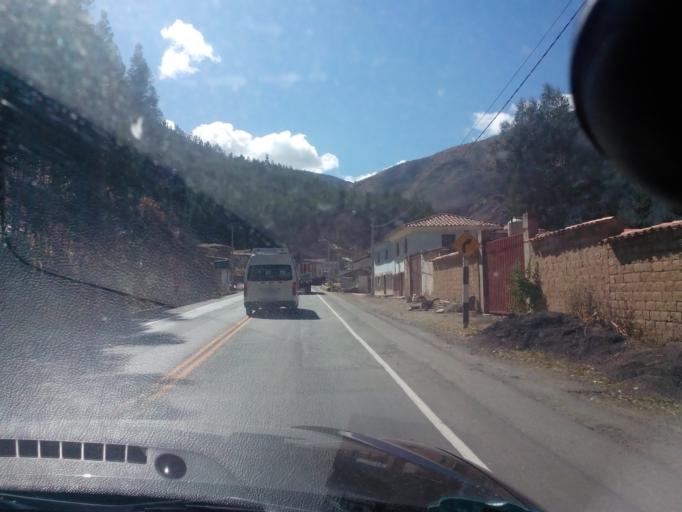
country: PE
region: Cusco
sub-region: Provincia de Quispicanchis
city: Urcos
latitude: -13.6877
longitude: -71.6003
